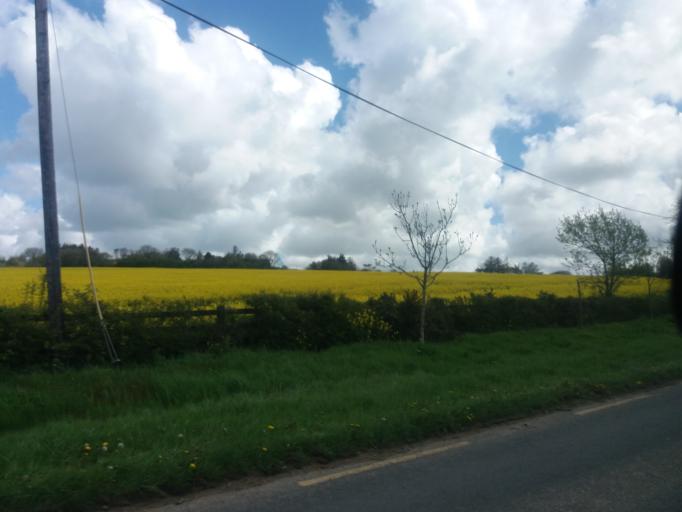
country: IE
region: Leinster
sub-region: Loch Garman
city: Loch Garman
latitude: 52.2893
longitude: -6.5973
